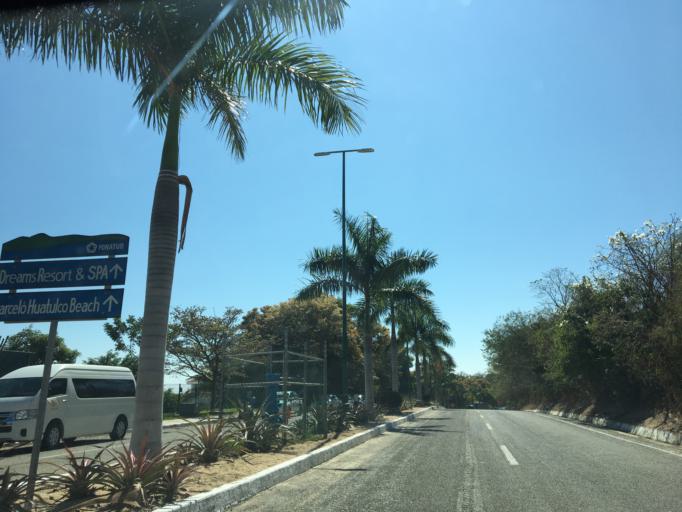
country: MX
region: Oaxaca
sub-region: Santa Maria Huatulco
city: Crucecita
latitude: 15.7832
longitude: -96.0672
